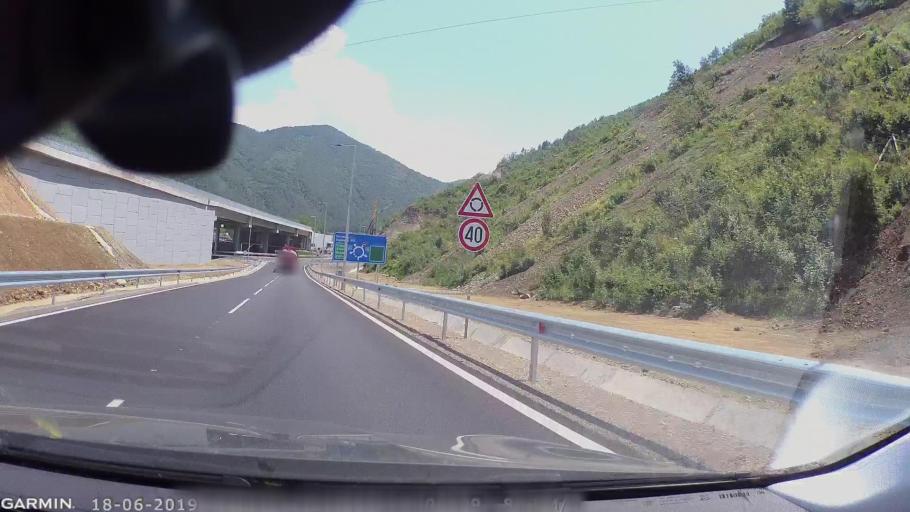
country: BG
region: Blagoevgrad
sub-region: Obshtina Blagoevgrad
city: Blagoevgrad
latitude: 41.9625
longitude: 23.0977
